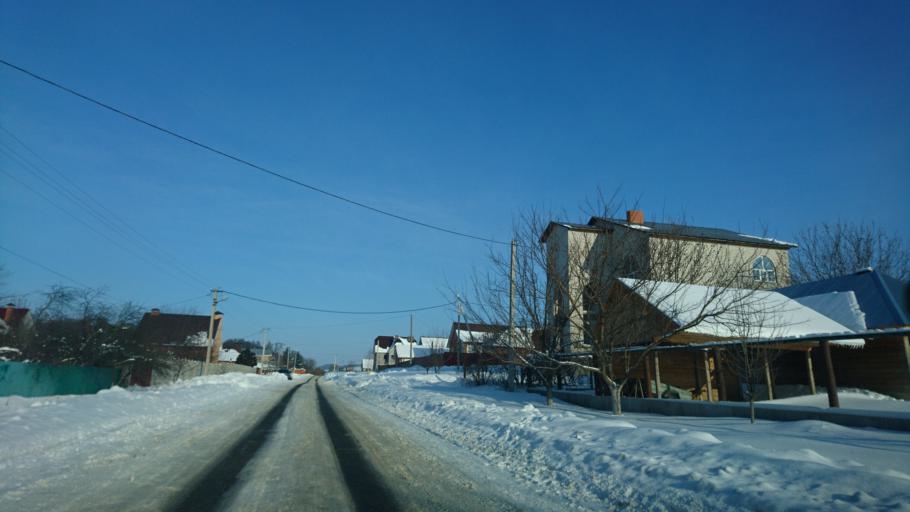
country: RU
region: Belgorod
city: Severnyy
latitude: 50.7227
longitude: 36.6103
